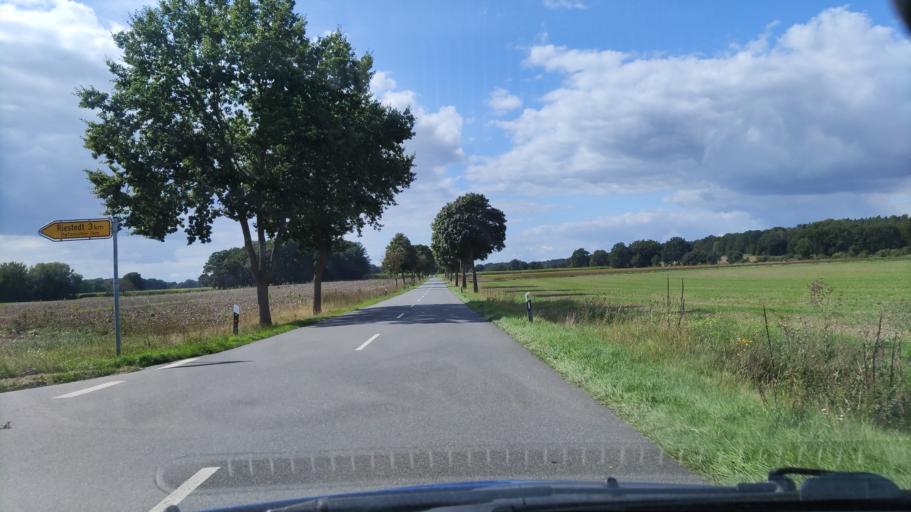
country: DE
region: Lower Saxony
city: Oetzen
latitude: 53.0214
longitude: 10.6619
